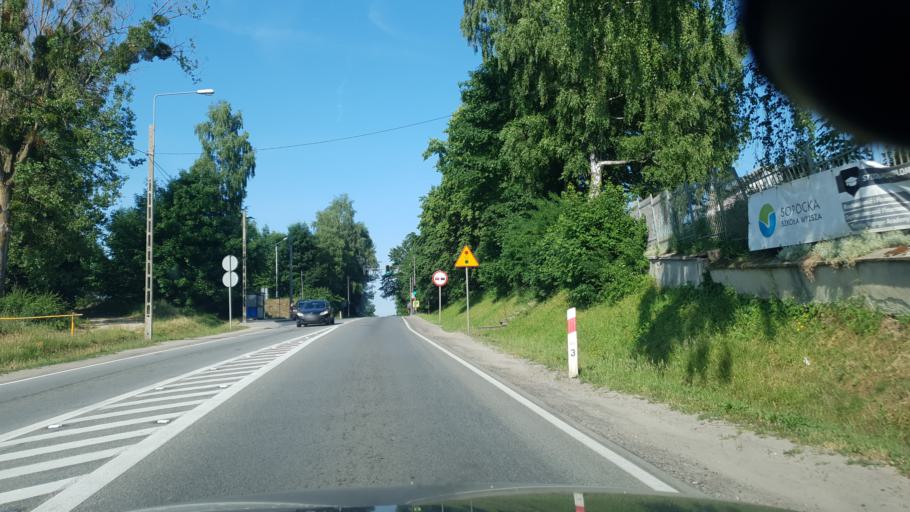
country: PL
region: Pomeranian Voivodeship
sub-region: Powiat kartuski
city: Chwaszczyno
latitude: 54.4513
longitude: 18.4386
